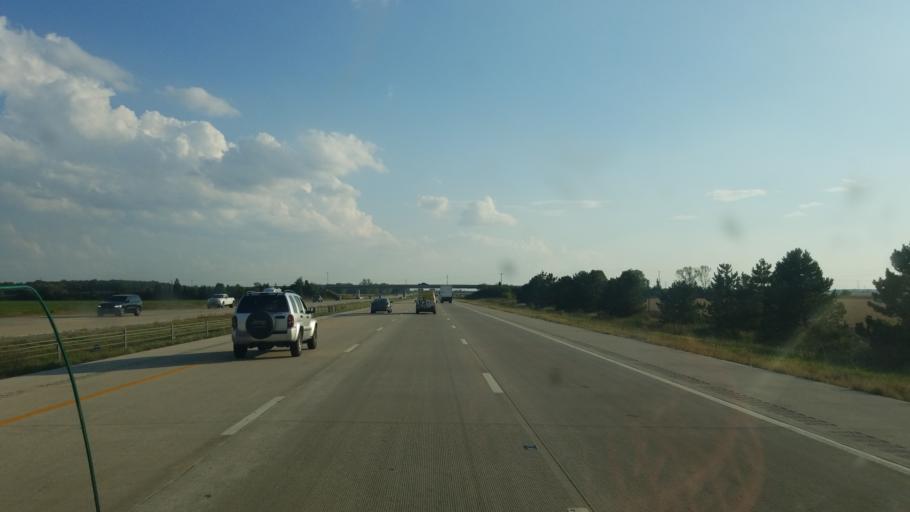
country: US
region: Ohio
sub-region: Wood County
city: Perrysburg
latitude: 41.4961
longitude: -83.6222
